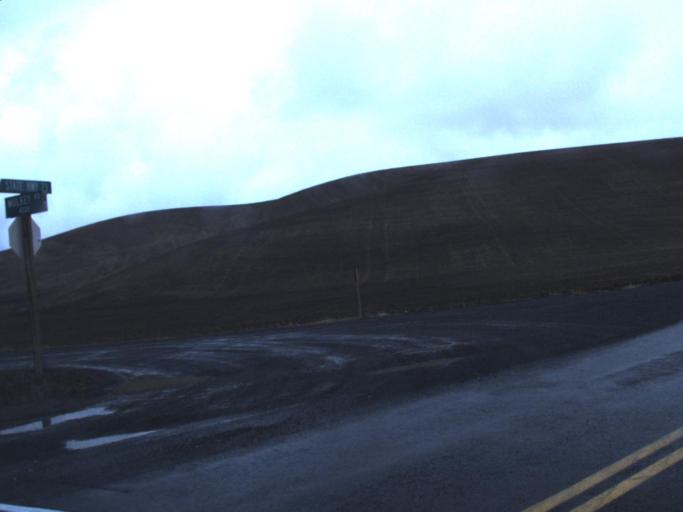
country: US
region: Washington
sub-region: Whitman County
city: Colfax
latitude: 47.0151
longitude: -117.4906
